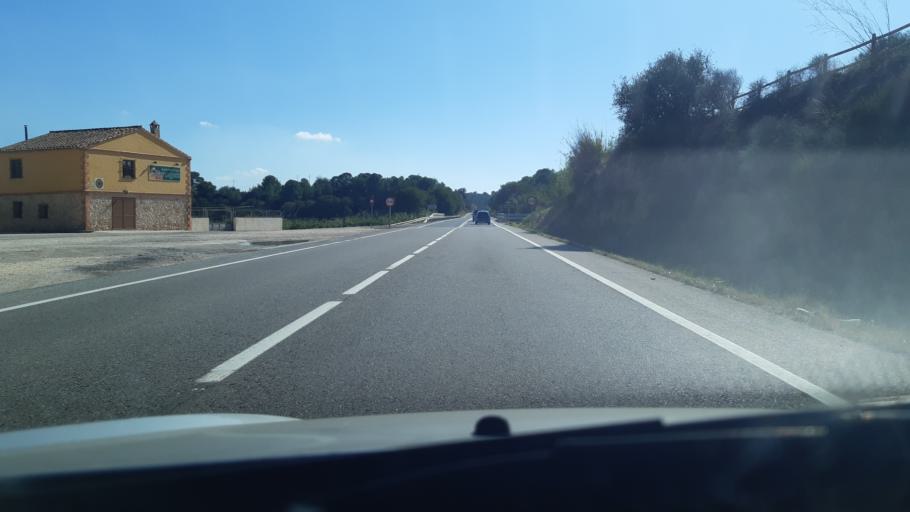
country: ES
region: Catalonia
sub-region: Provincia de Tarragona
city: Tivenys
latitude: 40.8922
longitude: 0.4897
